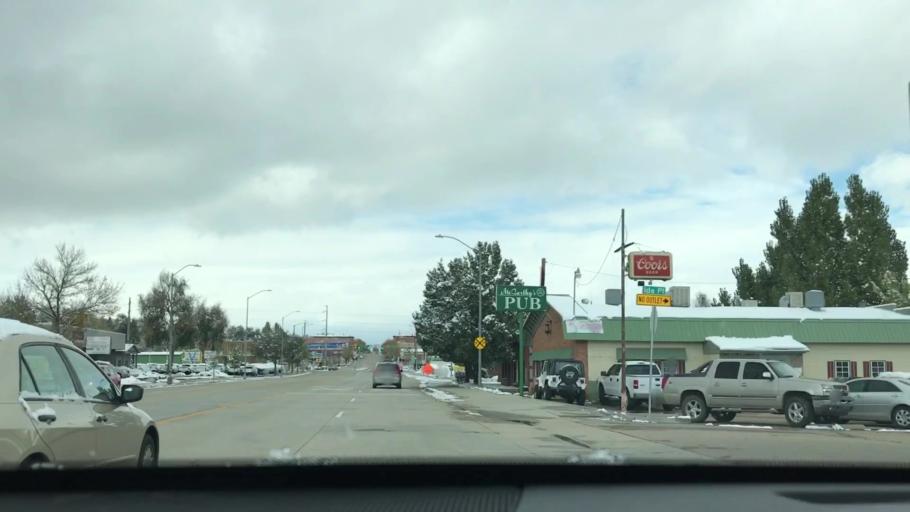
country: US
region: Colorado
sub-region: Boulder County
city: Longmont
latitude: 40.1582
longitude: -105.1025
